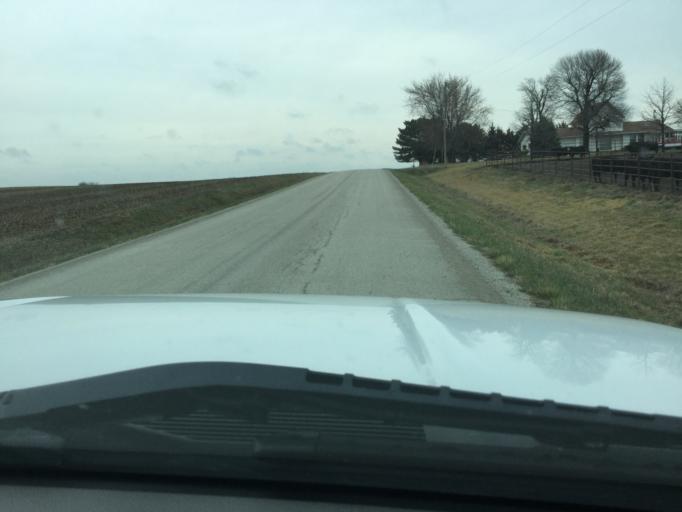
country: US
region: Kansas
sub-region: Nemaha County
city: Sabetha
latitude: 39.8436
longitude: -95.7142
